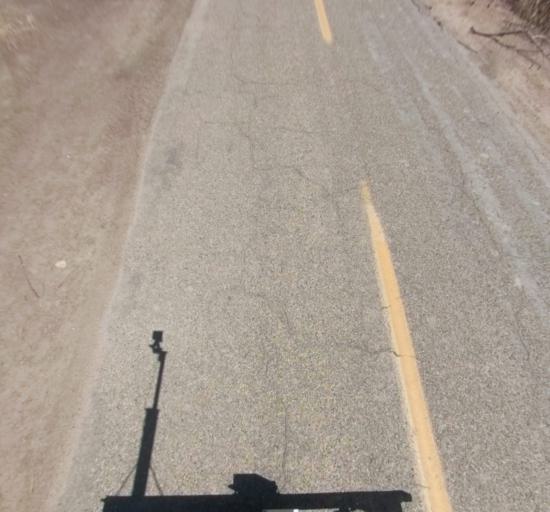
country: US
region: California
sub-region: Madera County
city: Chowchilla
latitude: 37.0745
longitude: -120.3107
